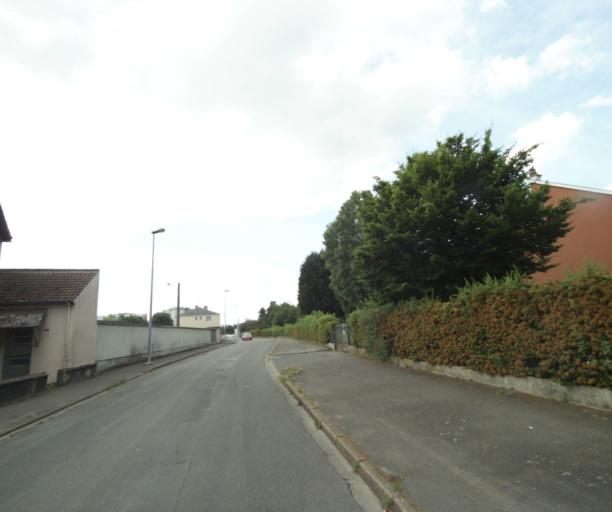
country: FR
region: Centre
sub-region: Departement d'Eure-et-Loir
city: Luisant
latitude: 48.4331
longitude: 1.4705
